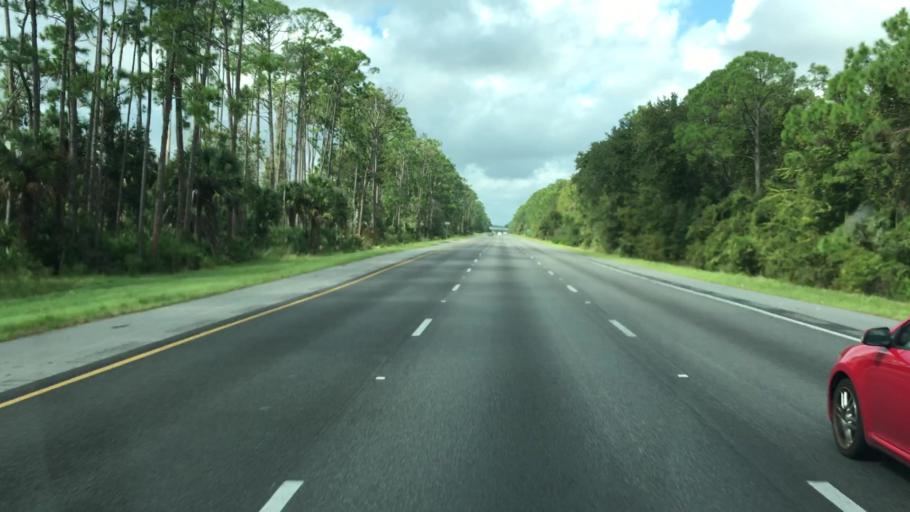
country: US
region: Florida
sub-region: Volusia County
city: Port Orange
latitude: 29.1147
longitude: -81.0348
